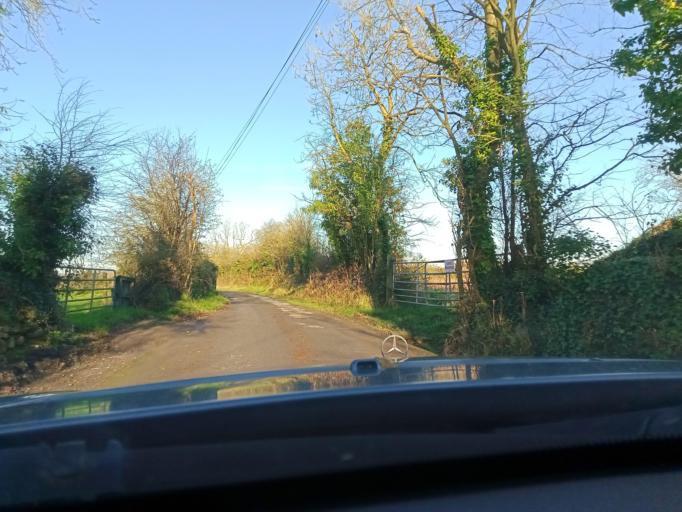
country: IE
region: Leinster
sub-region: Kilkenny
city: Mooncoin
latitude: 52.2902
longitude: -7.2056
